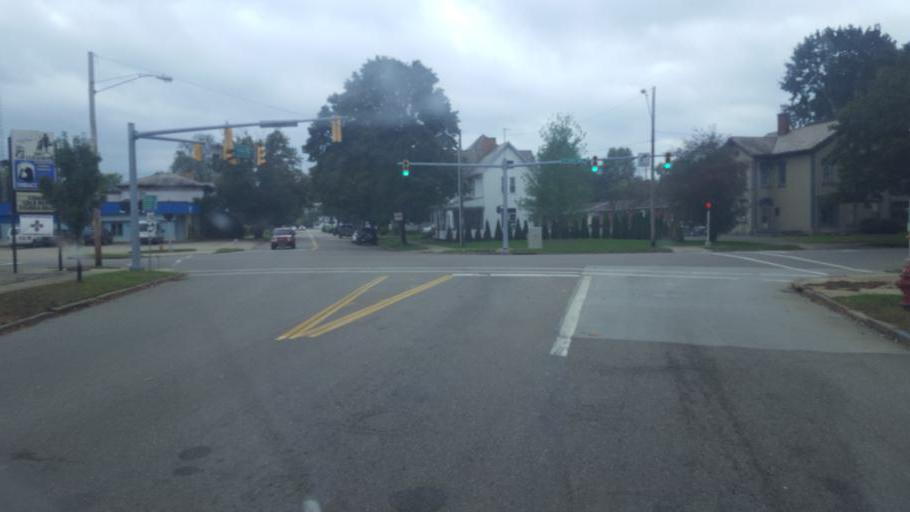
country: US
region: Ohio
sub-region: Tuscarawas County
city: New Philadelphia
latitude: 40.4888
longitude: -81.4390
